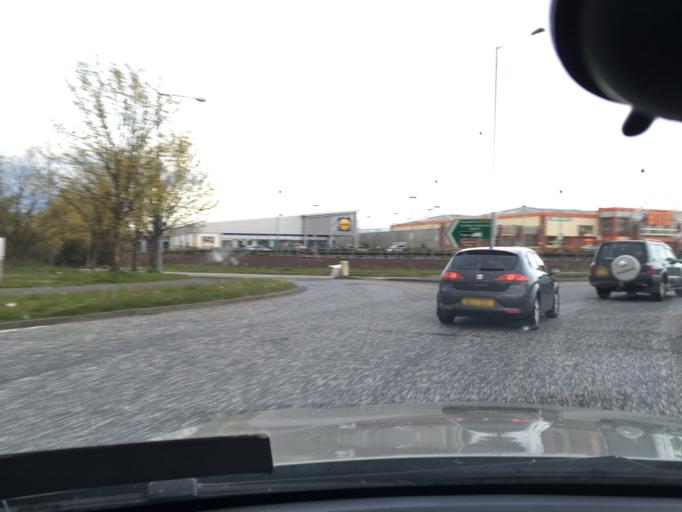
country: GB
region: Northern Ireland
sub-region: Newry and Mourne District
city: Newry
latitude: 54.1924
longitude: -6.3514
